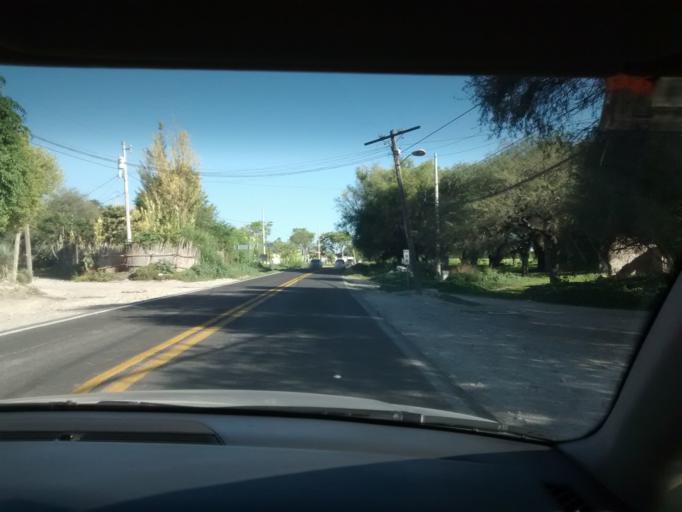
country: MX
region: Puebla
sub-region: Tepanco de Lopez
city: San Andres Cacaloapan
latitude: 18.5616
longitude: -97.5681
